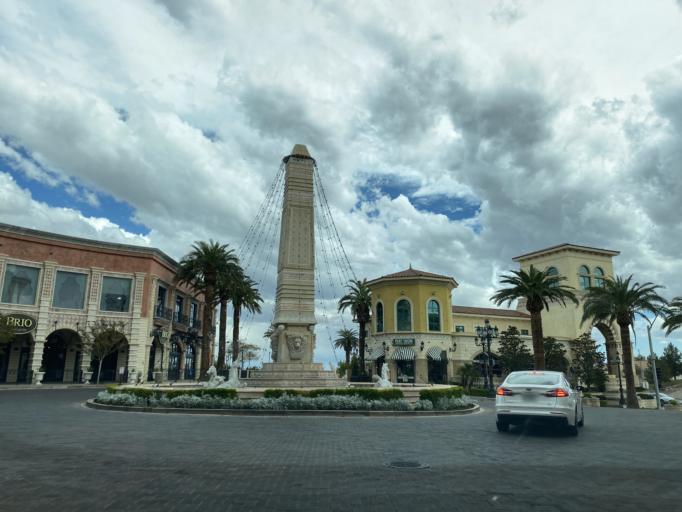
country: US
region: Nevada
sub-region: Clark County
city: Summerlin South
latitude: 36.1668
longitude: -115.2861
